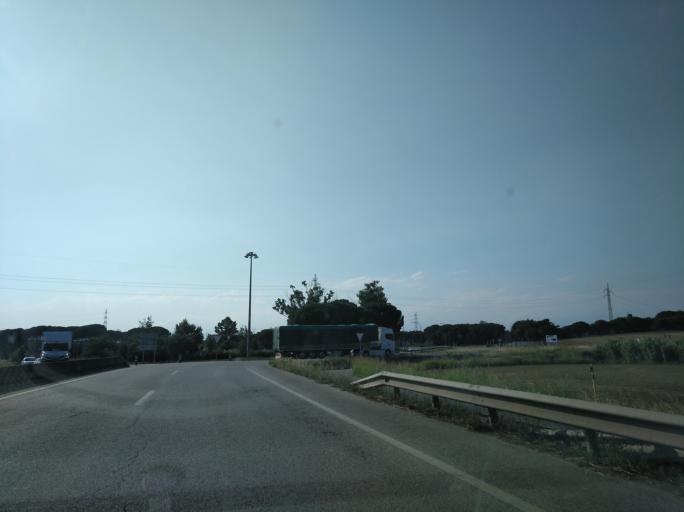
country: ES
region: Catalonia
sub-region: Provincia de Girona
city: Riudellots de la Selva
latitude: 41.8923
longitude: 2.7803
